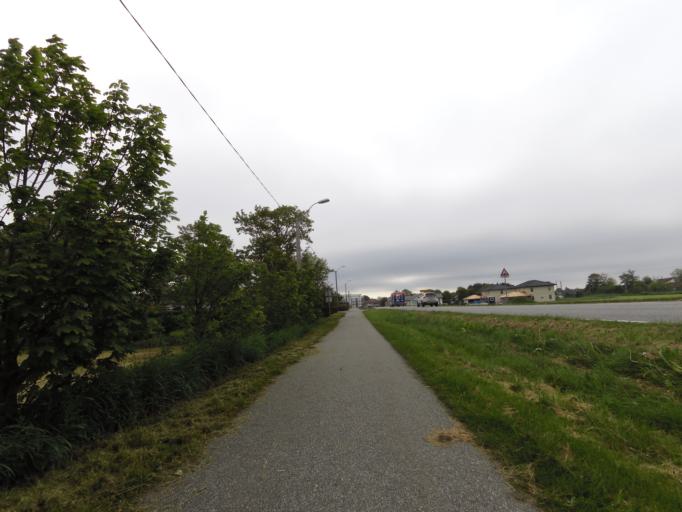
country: NO
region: Rogaland
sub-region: Ha
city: Vigrestad
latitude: 58.5729
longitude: 5.6828
